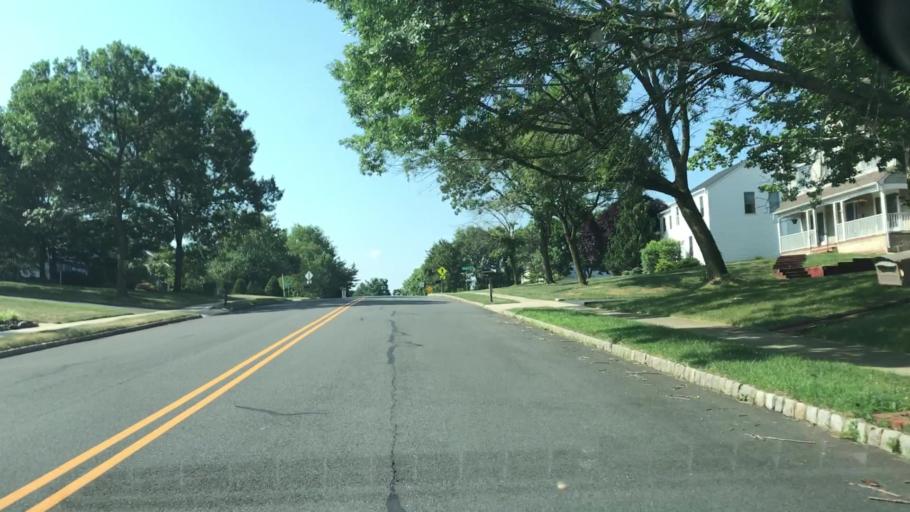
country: US
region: New Jersey
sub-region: Hunterdon County
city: Flemington
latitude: 40.5007
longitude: -74.8448
